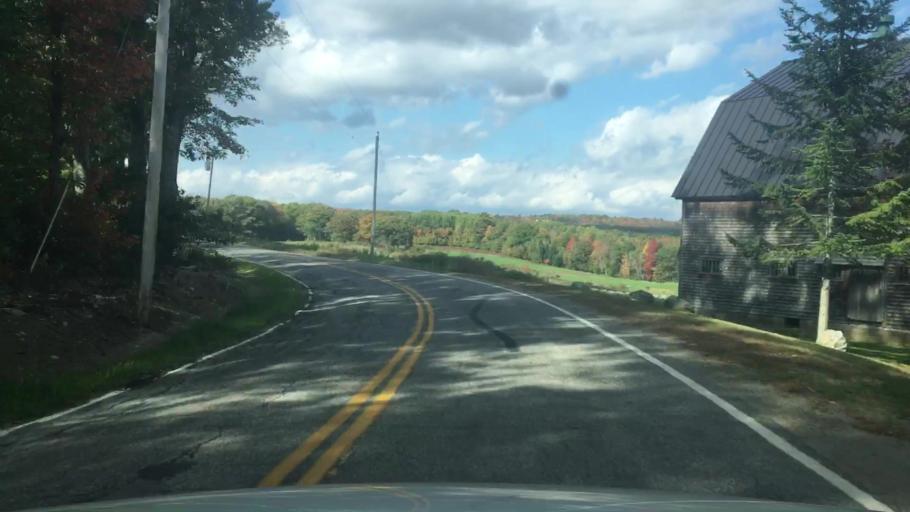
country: US
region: Maine
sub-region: Knox County
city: Appleton
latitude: 44.2640
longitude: -69.2749
